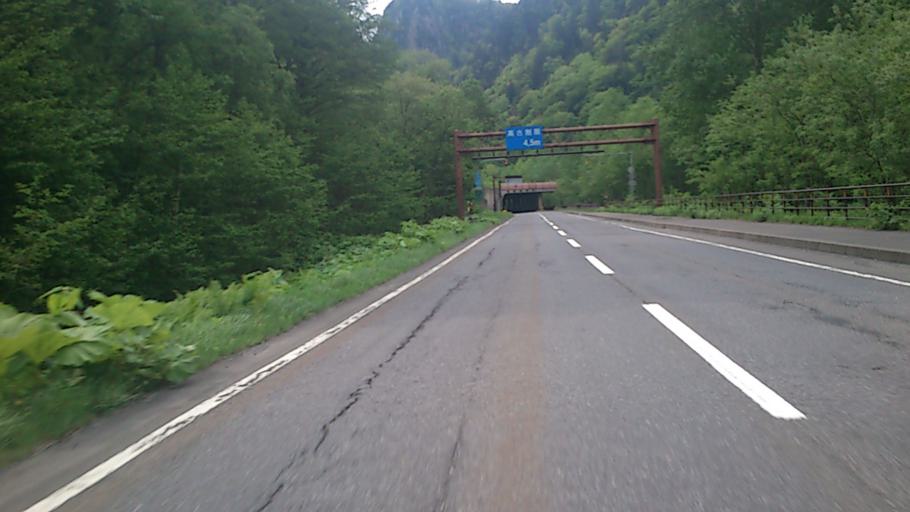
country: JP
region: Hokkaido
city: Kamikawa
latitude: 43.7455
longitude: 142.9351
